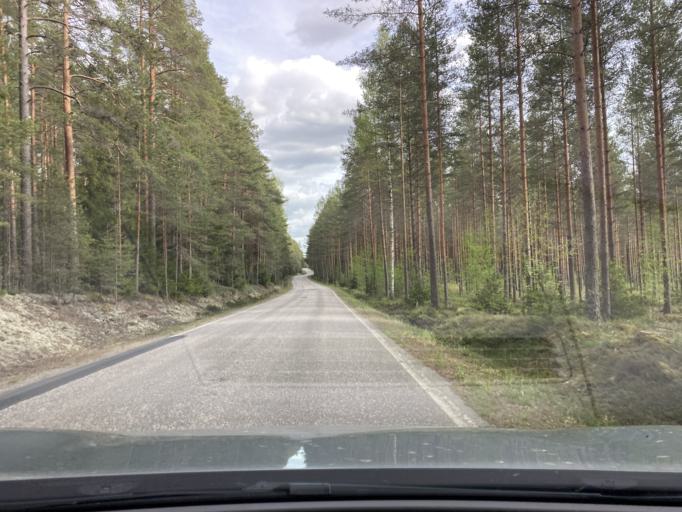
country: FI
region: Varsinais-Suomi
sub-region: Salo
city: Kiikala
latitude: 60.5023
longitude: 23.5477
